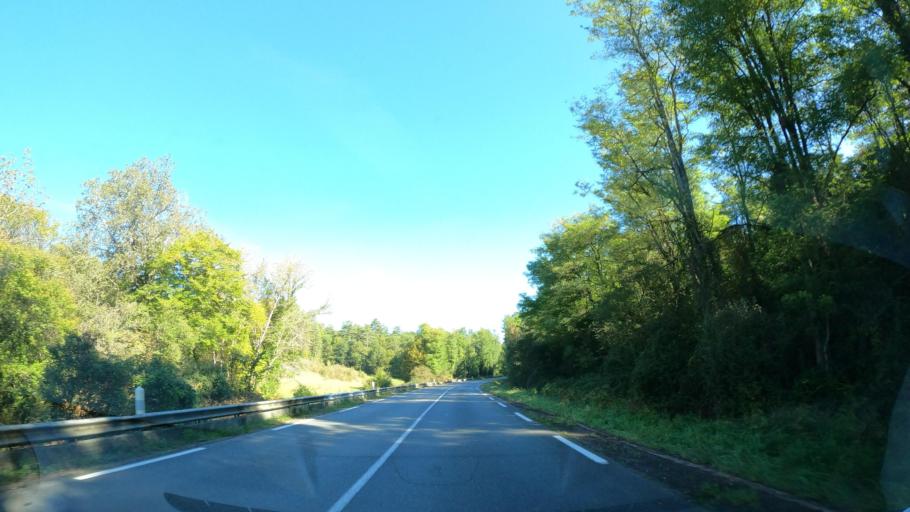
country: FR
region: Aquitaine
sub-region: Departement de la Dordogne
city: Notre-Dame-de-Sanilhac
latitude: 45.0877
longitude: 0.6897
